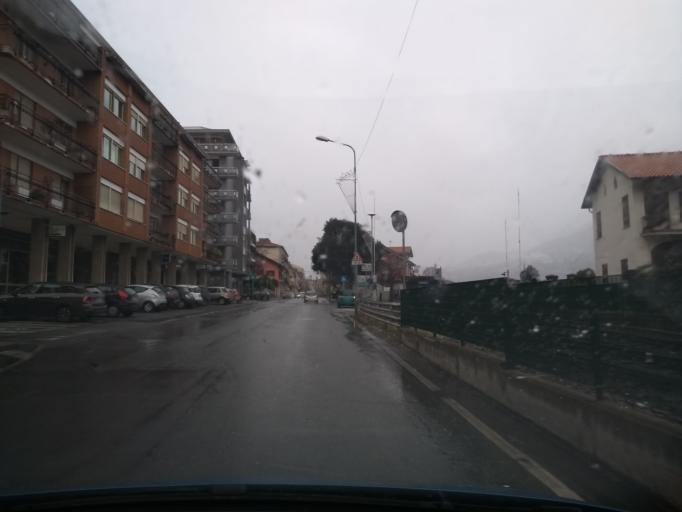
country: IT
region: Piedmont
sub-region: Provincia di Torino
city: Cuorgne
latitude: 45.3879
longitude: 7.6560
